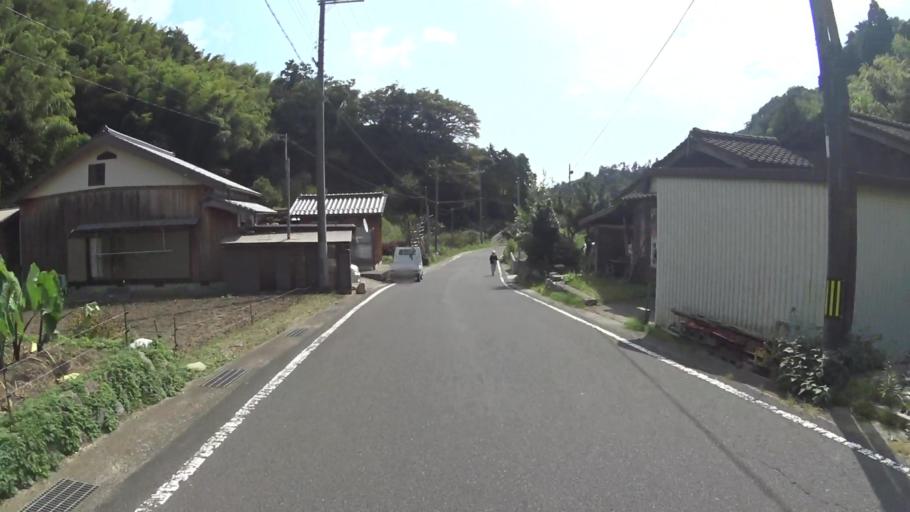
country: JP
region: Kyoto
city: Miyazu
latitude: 35.6698
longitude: 135.2452
